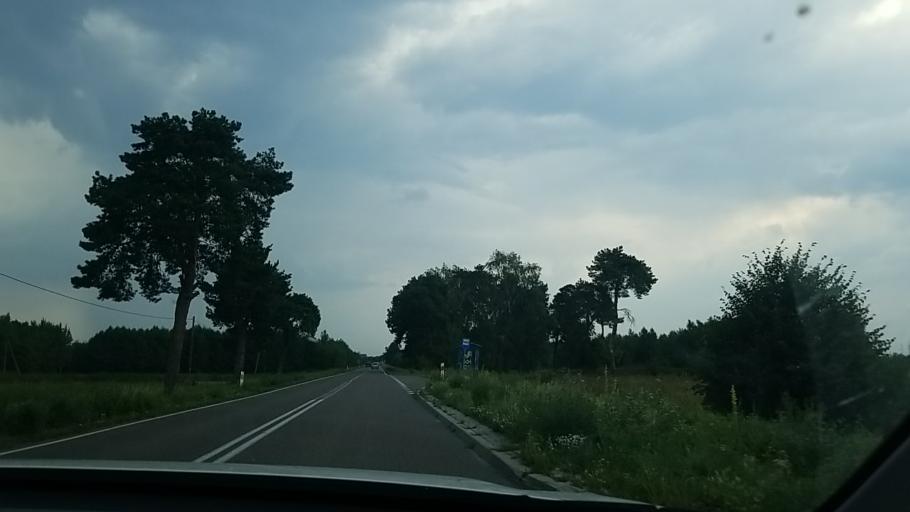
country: PL
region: Lublin Voivodeship
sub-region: Powiat swidnicki
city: Trawniki
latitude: 51.1868
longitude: 23.0541
